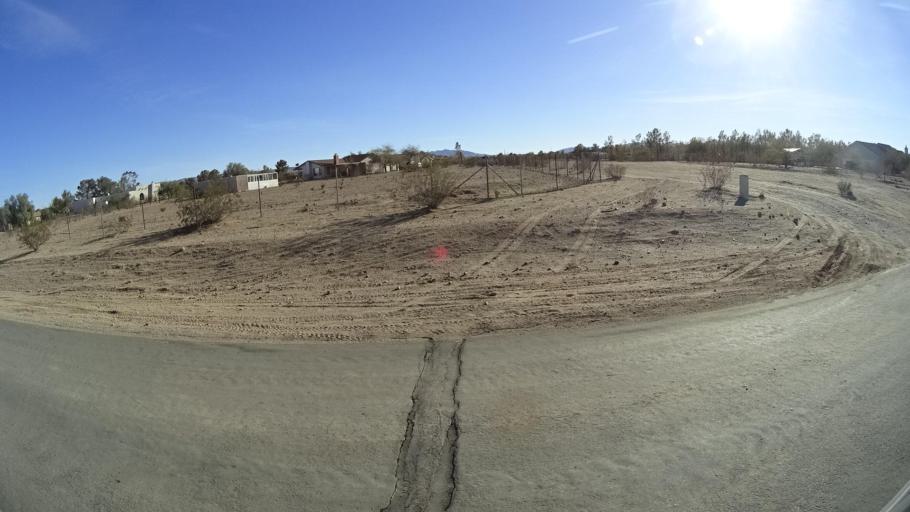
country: US
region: California
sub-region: Kern County
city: Ridgecrest
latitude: 35.6299
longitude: -117.7141
